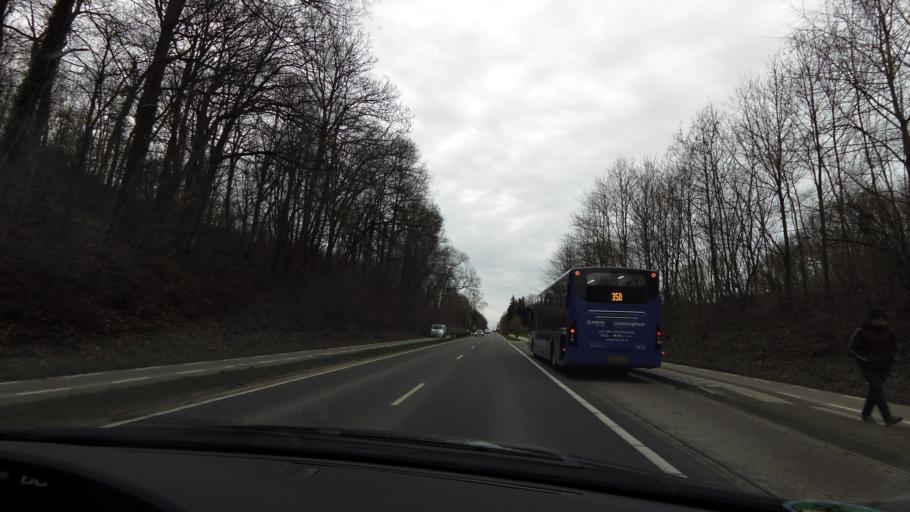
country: NL
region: Limburg
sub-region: Gemeente Maastricht
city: Heer
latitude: 50.8361
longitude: 5.7533
